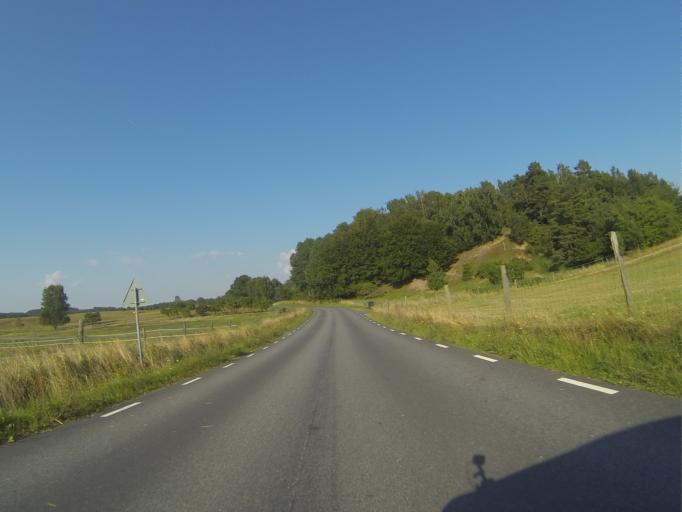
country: SE
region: Skane
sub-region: Lunds Kommun
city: Genarp
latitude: 55.5831
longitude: 13.3463
